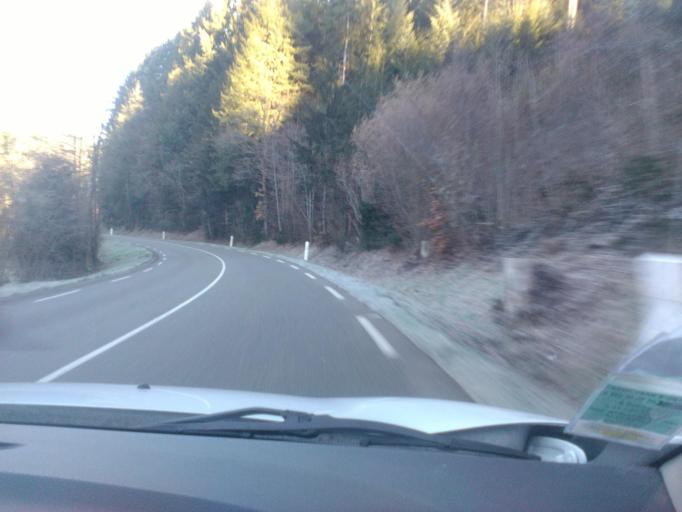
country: FR
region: Alsace
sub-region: Departement du Bas-Rhin
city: Rothau
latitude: 48.3781
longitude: 7.1428
